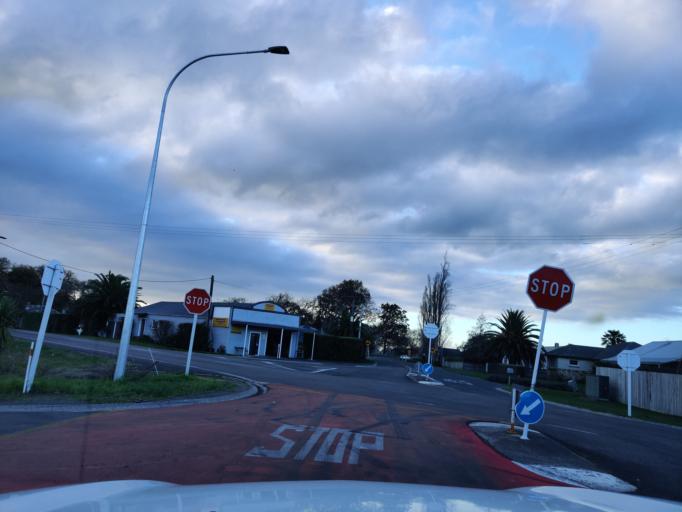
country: NZ
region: Waikato
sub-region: Waipa District
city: Cambridge
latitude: -37.8455
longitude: 175.4390
